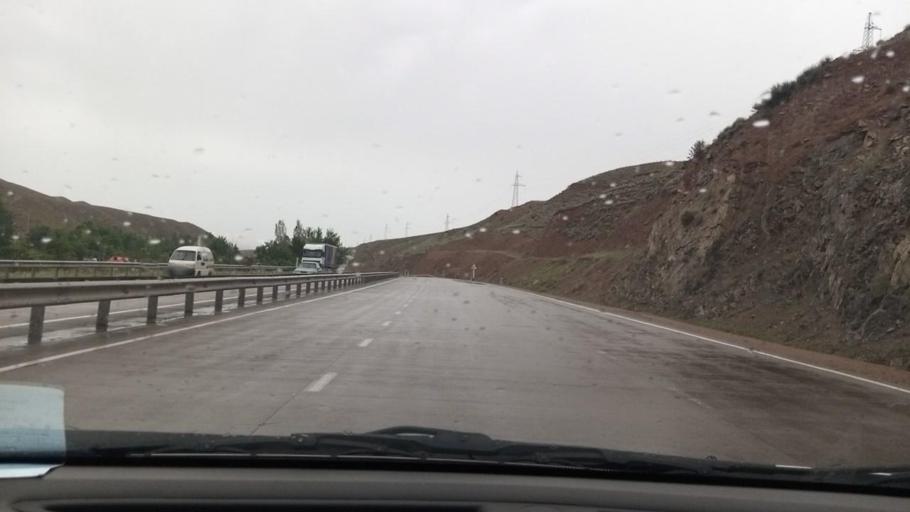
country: TJ
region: Viloyati Sughd
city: Shaydon
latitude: 40.9531
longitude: 70.6751
